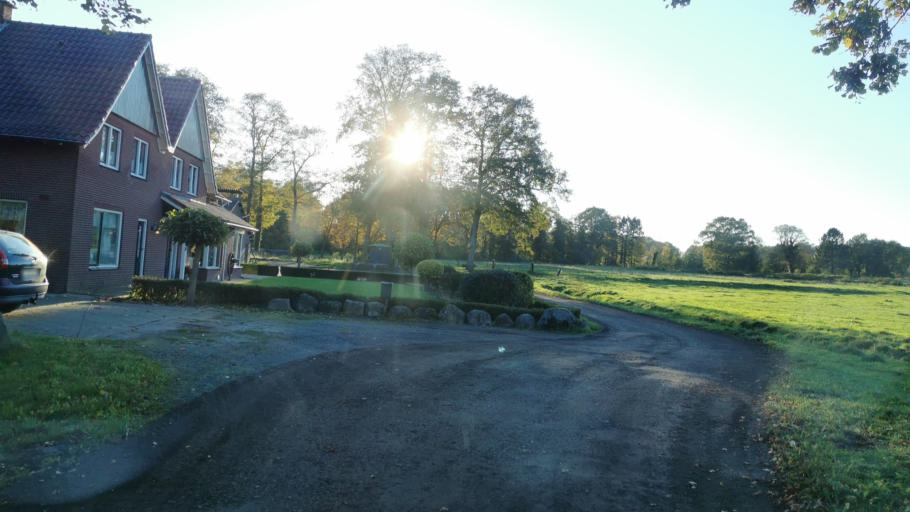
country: NL
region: Overijssel
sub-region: Gemeente Oldenzaal
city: Oldenzaal
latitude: 52.3156
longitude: 6.9774
